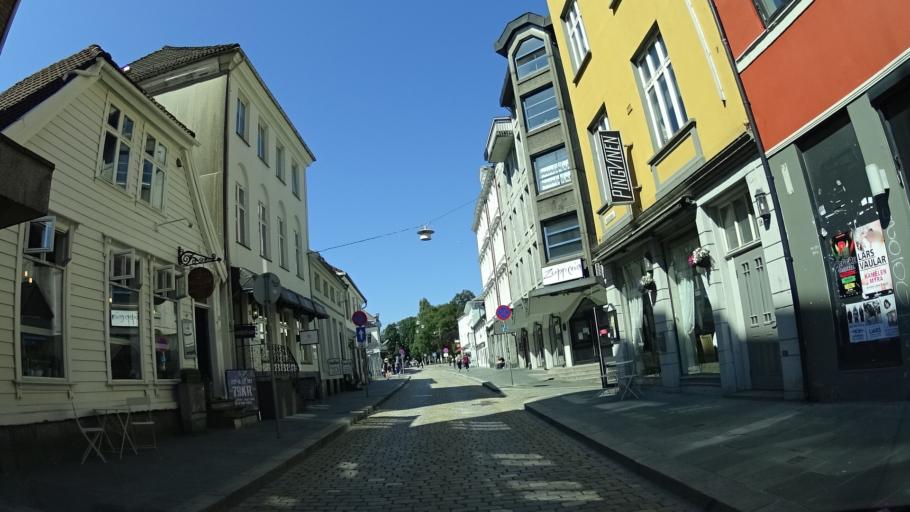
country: NO
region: Hordaland
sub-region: Bergen
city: Bergen
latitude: 60.3912
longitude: 5.3219
